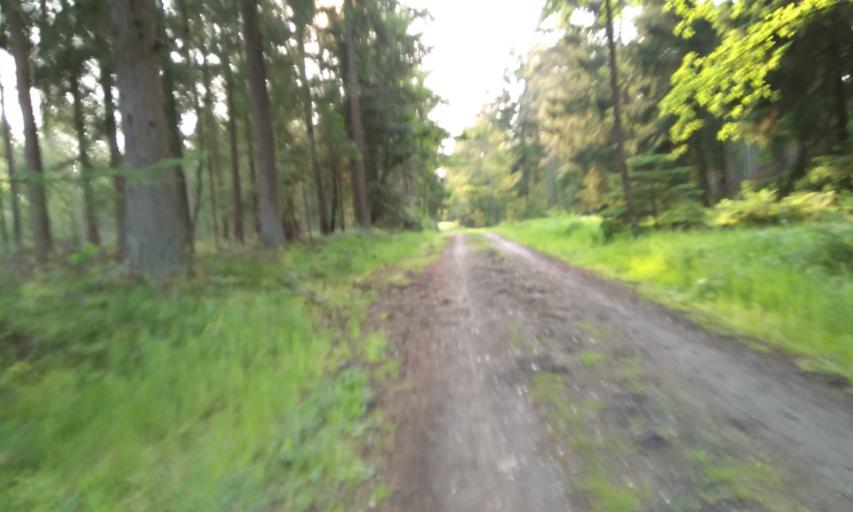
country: DE
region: Lower Saxony
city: Agathenburg
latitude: 53.5302
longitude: 9.5083
